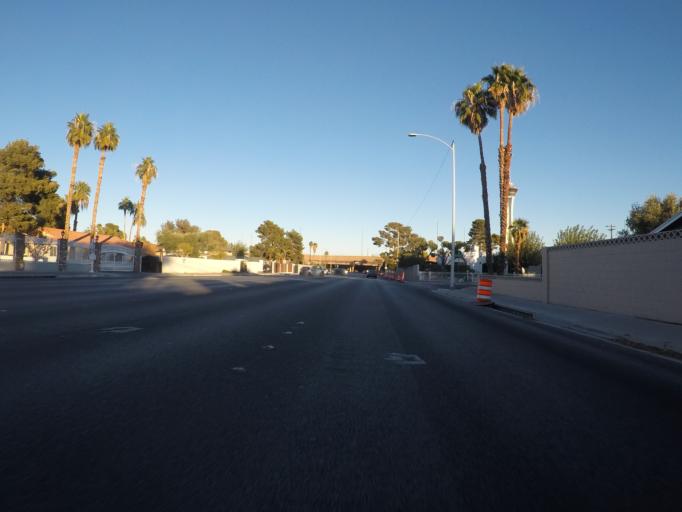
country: US
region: Nevada
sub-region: Clark County
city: Las Vegas
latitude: 36.1515
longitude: -115.1687
